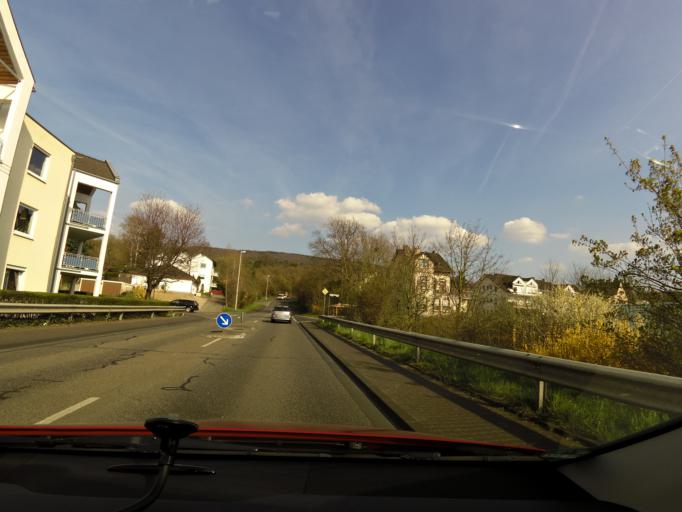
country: DE
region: Rheinland-Pfalz
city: Lahnstein
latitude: 50.3235
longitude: 7.5995
